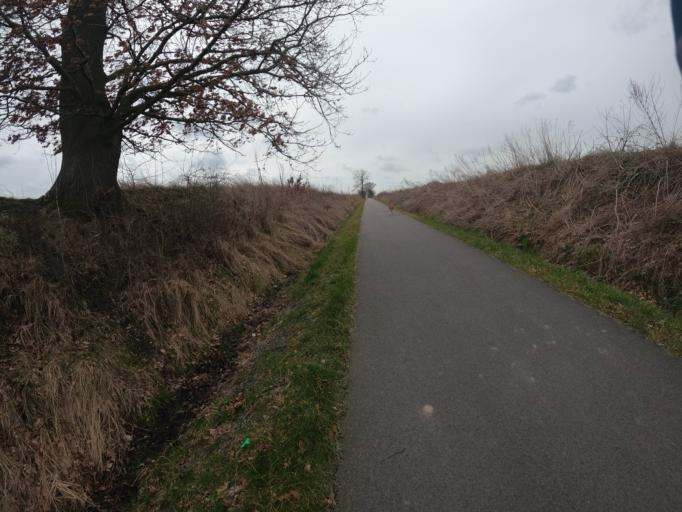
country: PL
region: West Pomeranian Voivodeship
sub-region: Powiat gryficki
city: Trzebiatow
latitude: 54.0870
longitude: 15.2664
